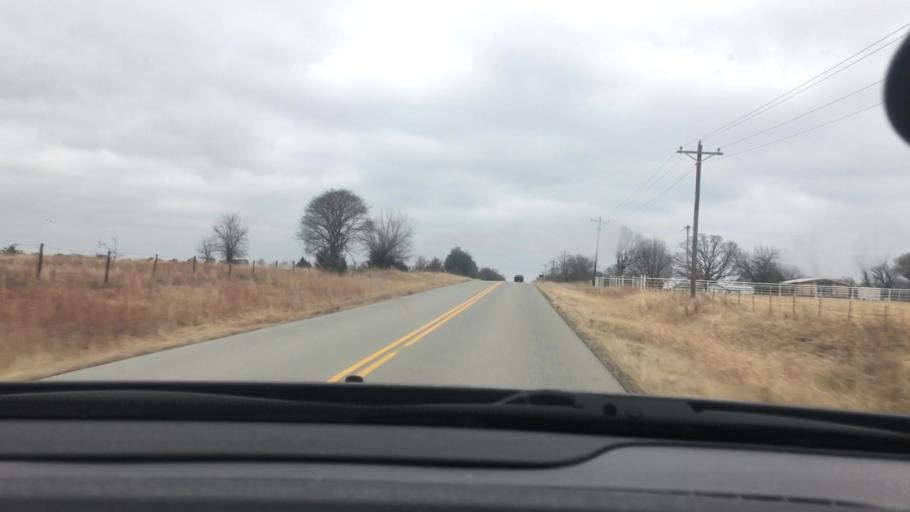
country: US
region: Oklahoma
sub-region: Atoka County
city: Atoka
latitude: 34.3349
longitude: -96.0754
